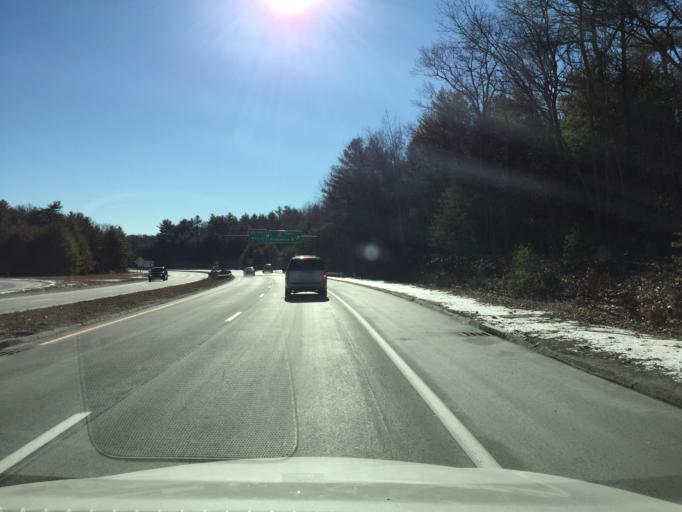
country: US
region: Massachusetts
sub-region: Norfolk County
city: Foxborough
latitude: 42.0468
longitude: -71.2454
